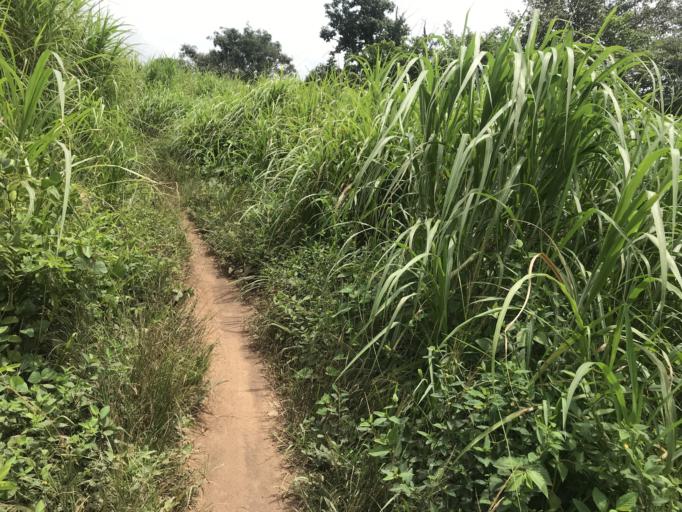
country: GN
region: Nzerekore
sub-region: Prefecture de Guekedou
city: Gueckedou
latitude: 8.4997
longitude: -10.3309
